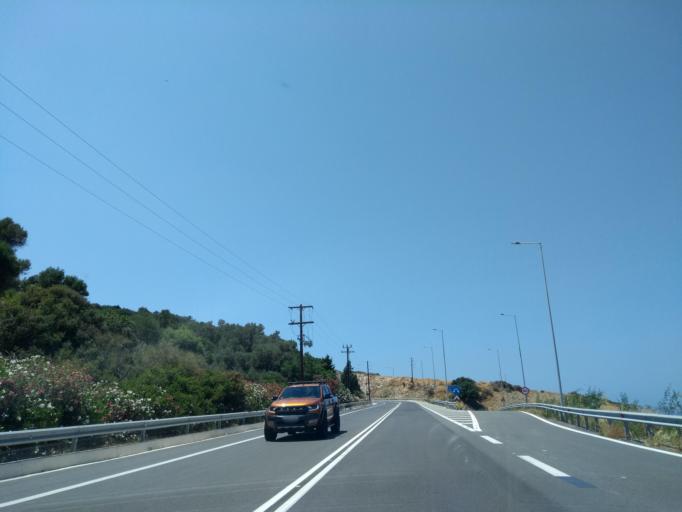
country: GR
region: Crete
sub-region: Nomos Irakleiou
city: Gazi
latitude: 35.4050
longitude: 24.9930
